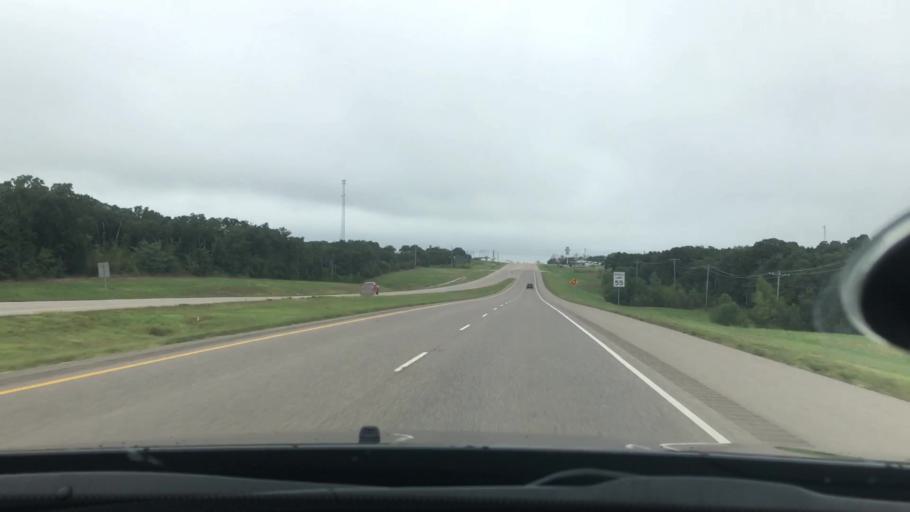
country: US
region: Oklahoma
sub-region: Lincoln County
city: Prague
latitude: 35.3721
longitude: -96.6714
